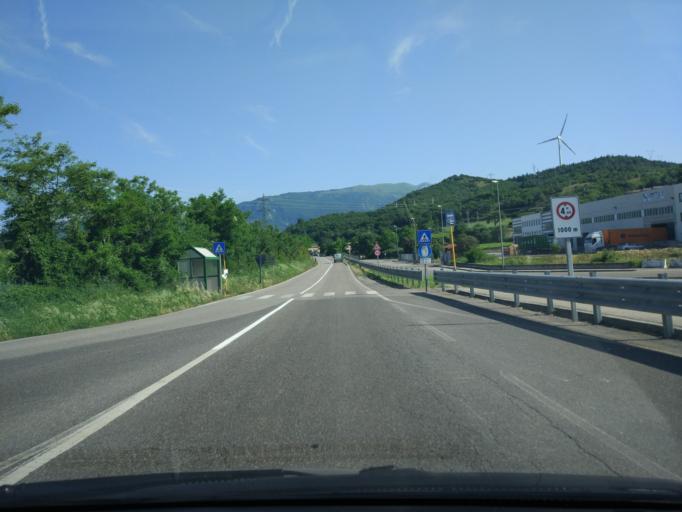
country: IT
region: Veneto
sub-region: Provincia di Verona
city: Affi
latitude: 45.5510
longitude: 10.8040
